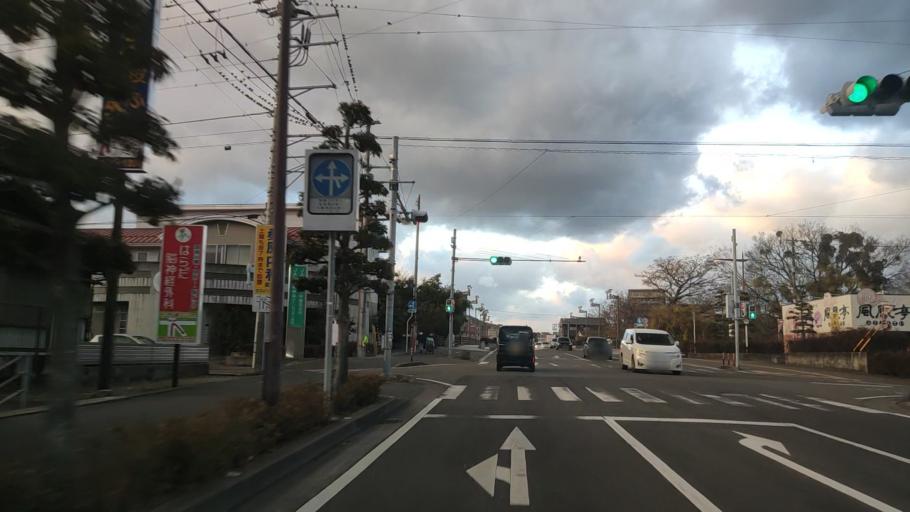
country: JP
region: Ehime
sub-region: Shikoku-chuo Shi
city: Matsuyama
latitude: 33.8386
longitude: 132.7863
